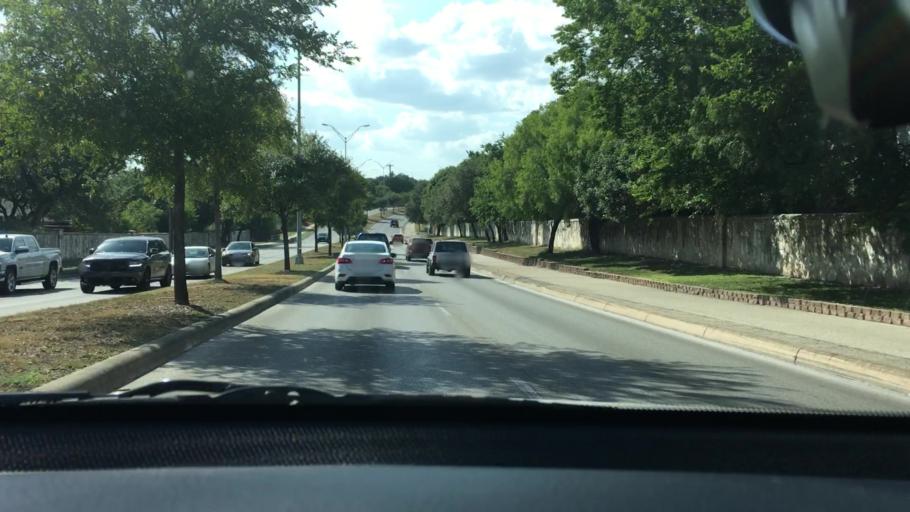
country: US
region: Texas
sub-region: Bexar County
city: Selma
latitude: 29.5827
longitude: -98.2835
